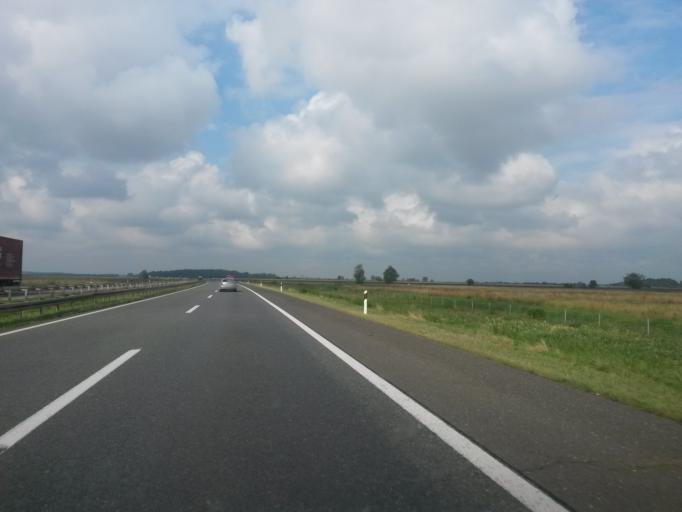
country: HR
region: Zagrebacka
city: Kriz
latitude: 45.6819
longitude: 16.4569
